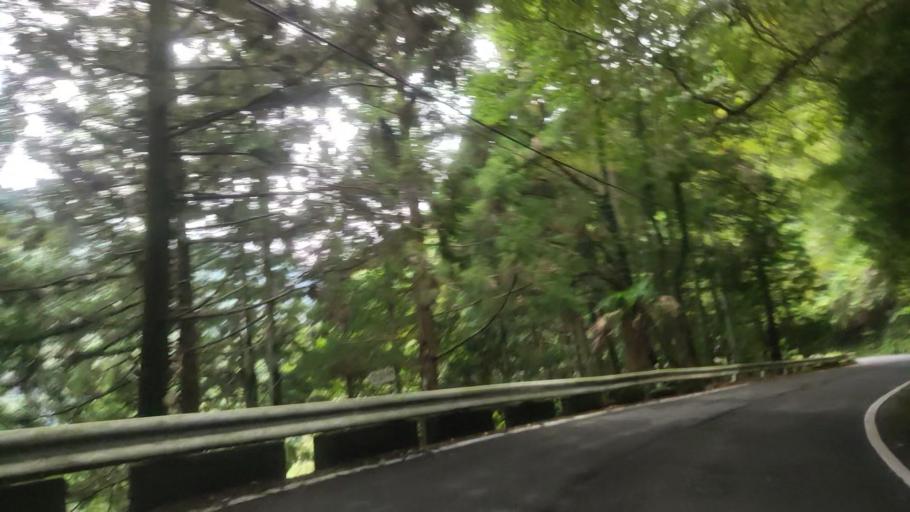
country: JP
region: Wakayama
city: Koya
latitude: 34.2489
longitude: 135.5453
